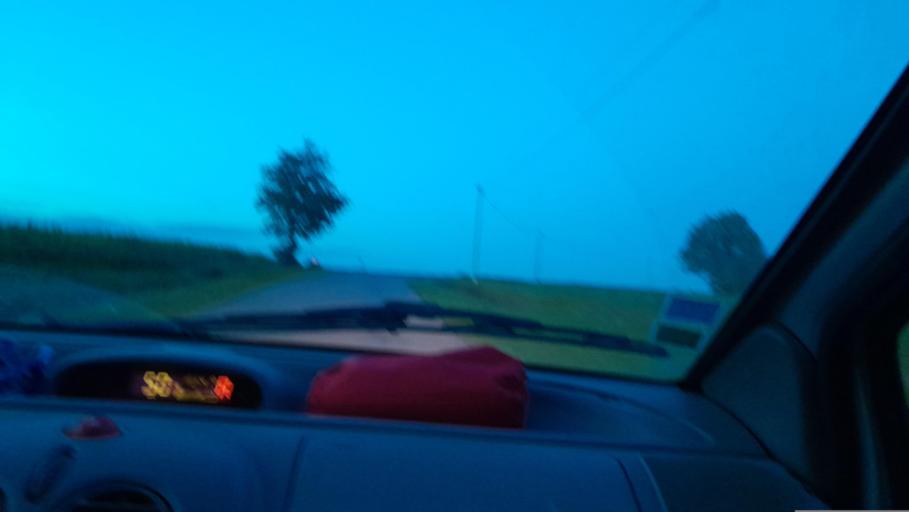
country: FR
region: Brittany
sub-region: Departement d'Ille-et-Vilaine
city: Rannee
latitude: 47.8701
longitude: -1.1888
